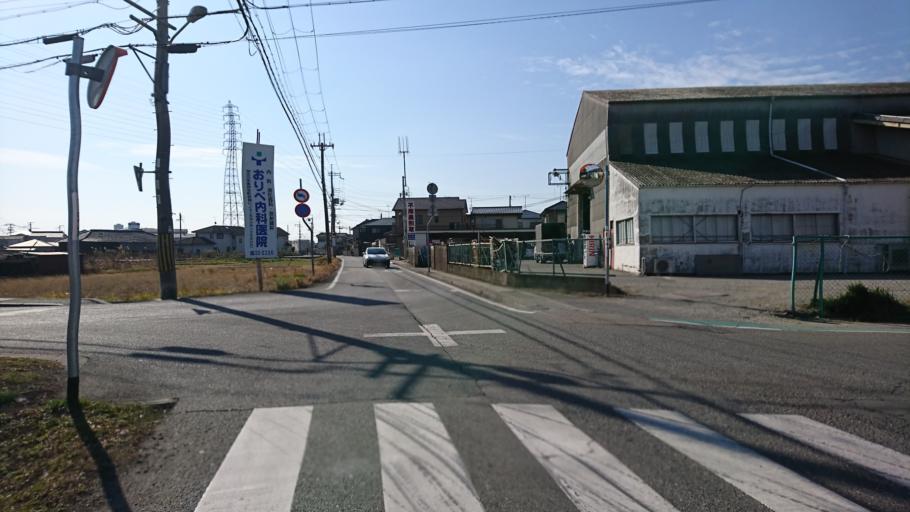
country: JP
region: Hyogo
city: Kakogawacho-honmachi
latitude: 34.7889
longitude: 134.8308
